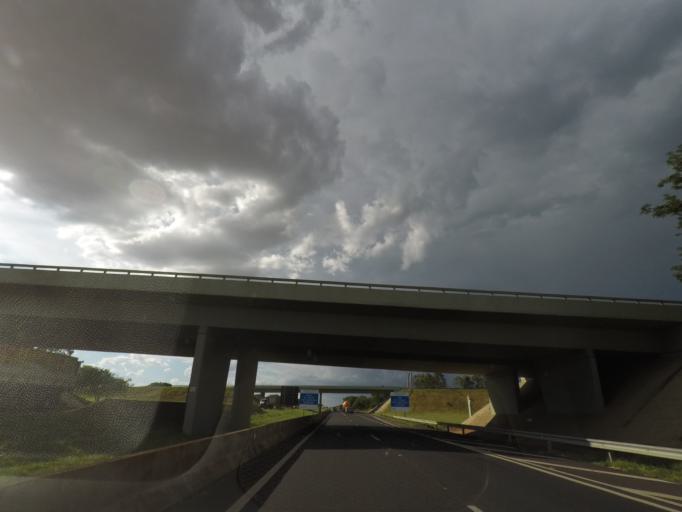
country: BR
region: Sao Paulo
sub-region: Ribeirao Preto
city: Ribeirao Preto
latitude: -21.1138
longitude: -47.7794
